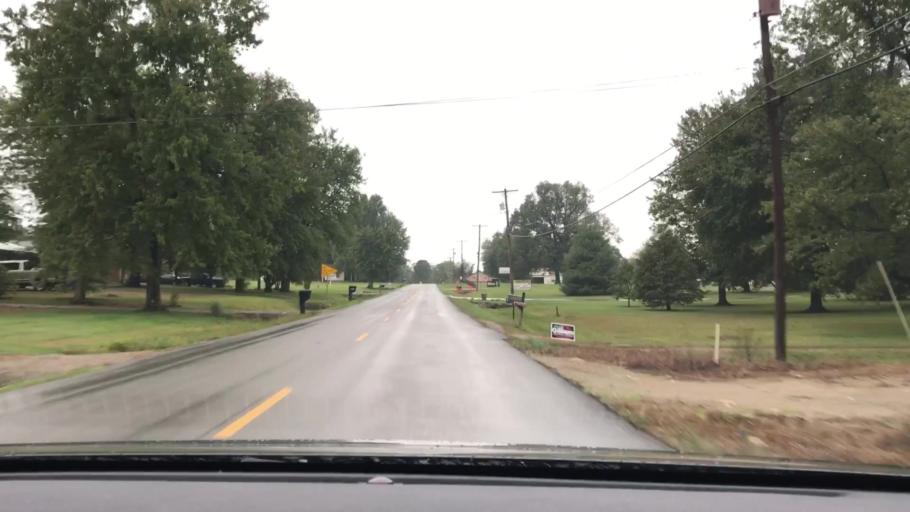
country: US
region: Kentucky
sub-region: Hopkins County
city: Madisonville
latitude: 37.3502
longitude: -87.3995
